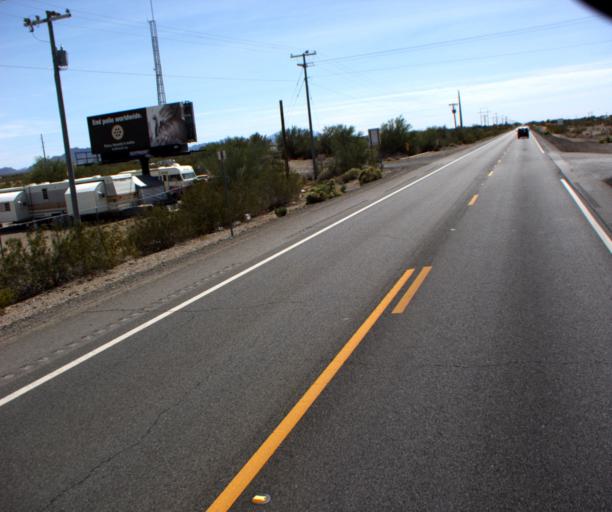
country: US
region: Arizona
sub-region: La Paz County
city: Quartzsite
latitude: 33.6575
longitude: -114.2171
